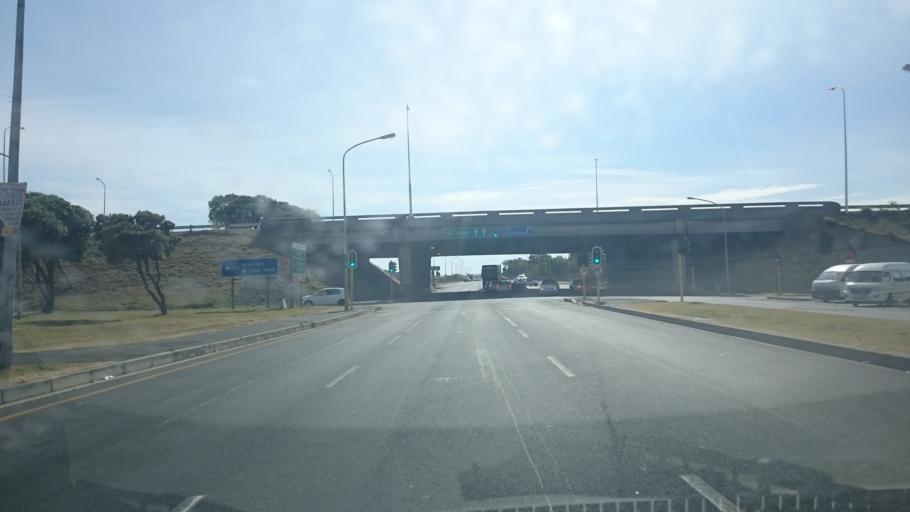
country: ZA
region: Western Cape
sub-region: City of Cape Town
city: Lansdowne
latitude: -34.0134
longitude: 18.4832
